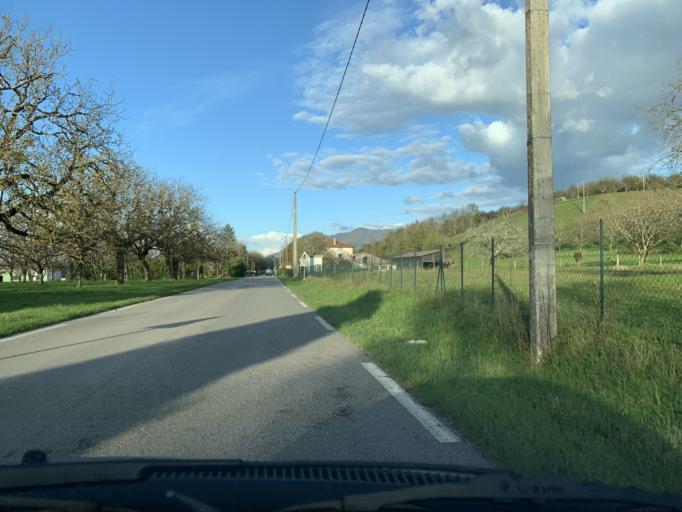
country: FR
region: Rhone-Alpes
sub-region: Departement de la Drome
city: Saint-Jean-en-Royans
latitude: 45.0260
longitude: 5.2978
